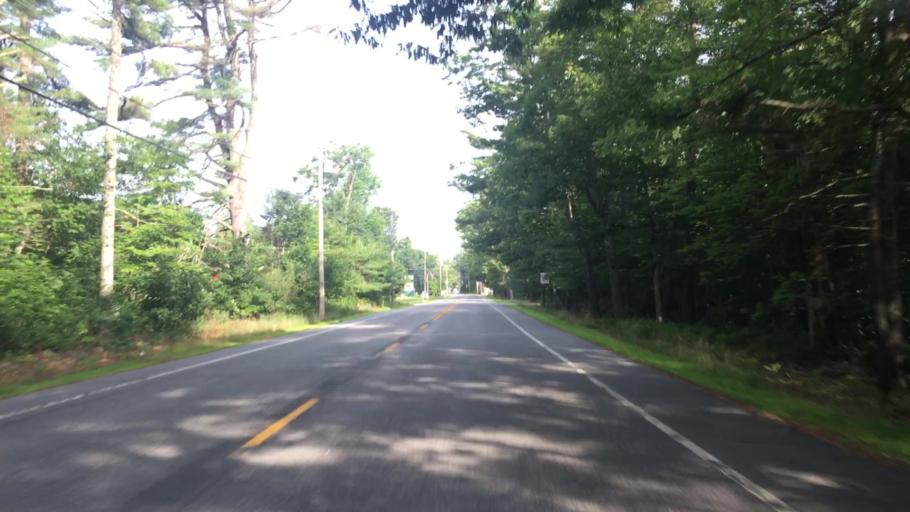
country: US
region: Maine
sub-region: York County
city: Cornish
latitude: 43.7995
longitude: -70.7854
